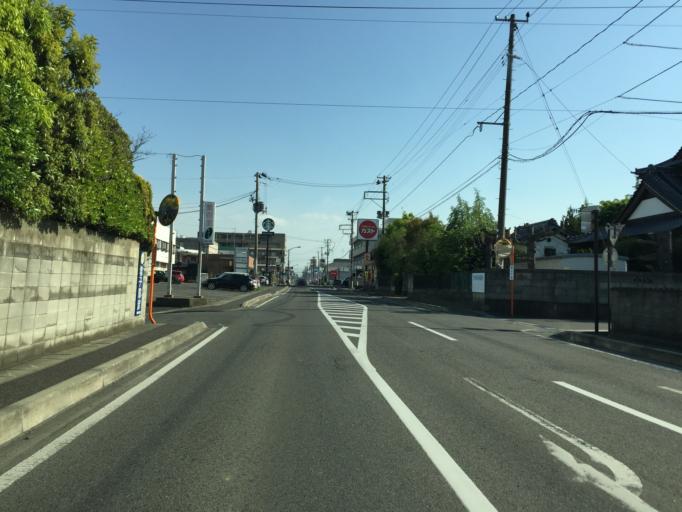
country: JP
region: Fukushima
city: Koriyama
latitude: 37.3986
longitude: 140.3341
